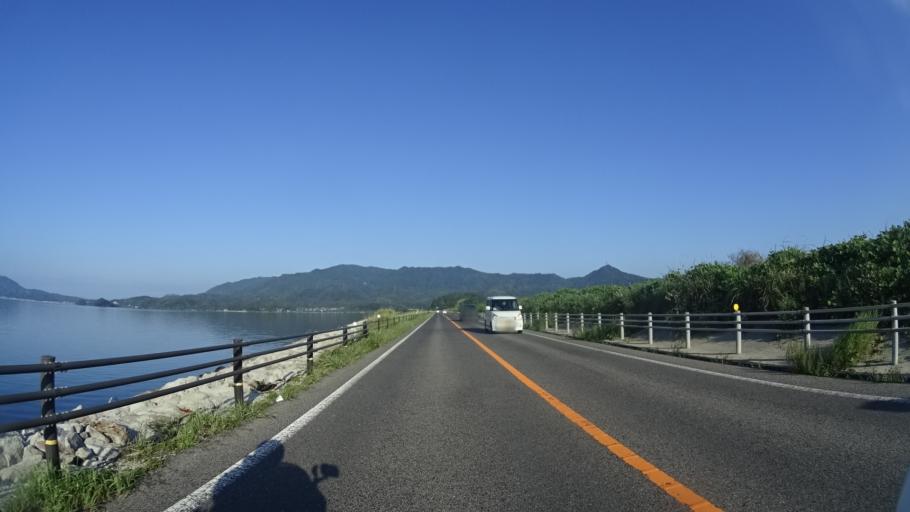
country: JP
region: Shimane
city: Sakaiminato
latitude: 35.5273
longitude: 133.1726
